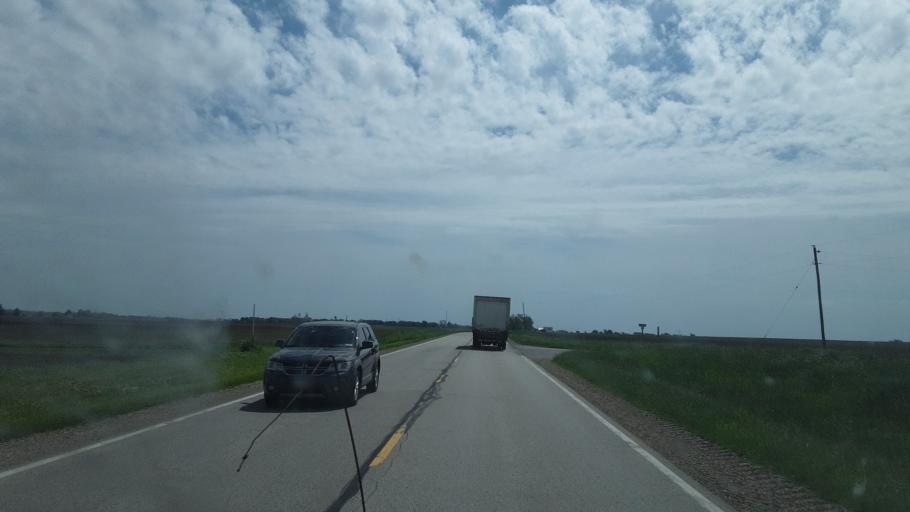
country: US
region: Illinois
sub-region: Logan County
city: Atlanta
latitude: 40.3113
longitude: -89.2072
